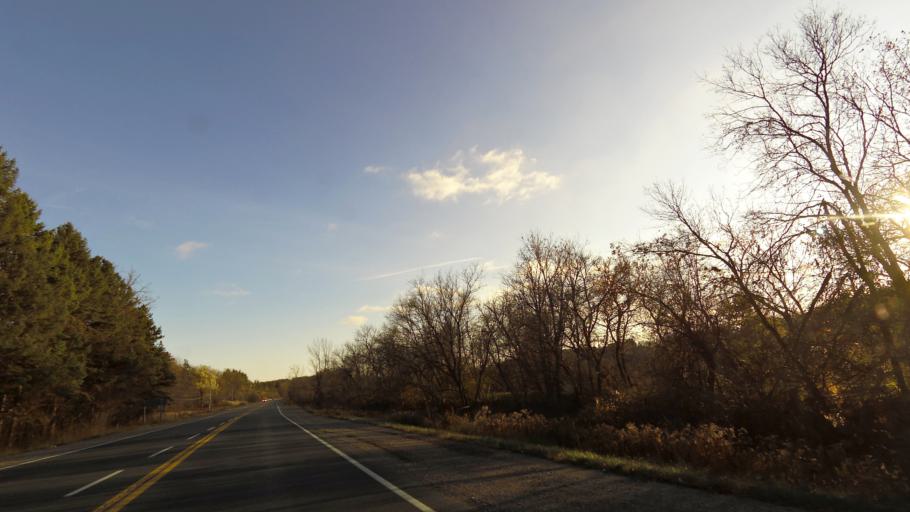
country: CA
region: Ontario
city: Cambridge
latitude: 43.3157
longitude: -80.3117
